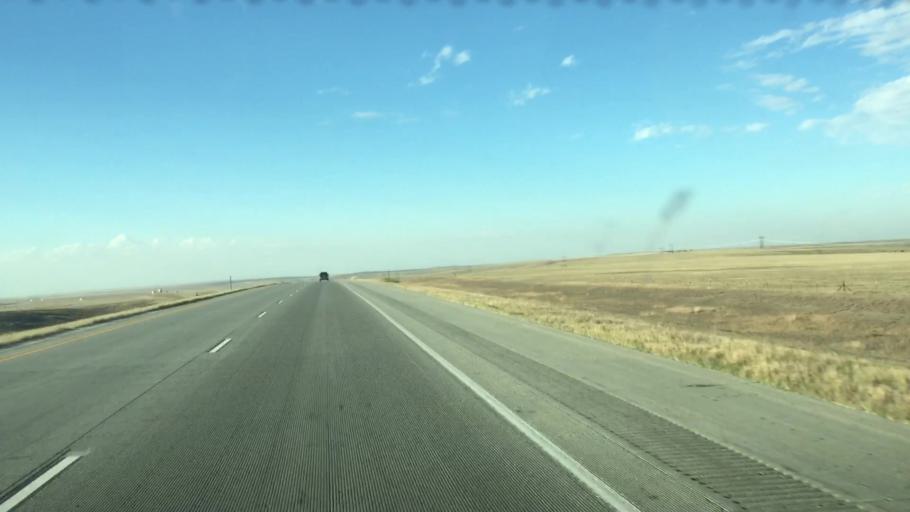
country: US
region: Colorado
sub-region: Lincoln County
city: Limon
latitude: 39.3914
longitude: -103.8892
